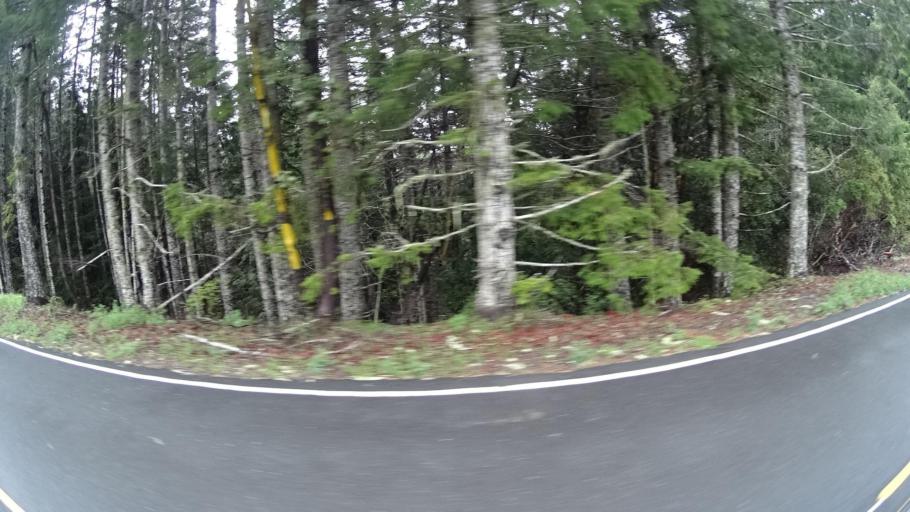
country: US
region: California
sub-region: Humboldt County
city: Westhaven-Moonstone
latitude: 41.1802
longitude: -123.9241
